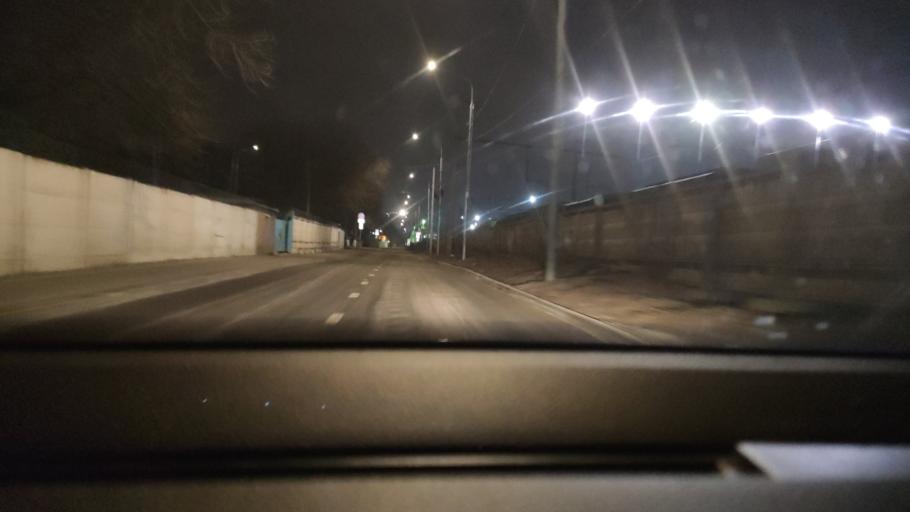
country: RU
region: Moscow
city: Lyublino
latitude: 55.6771
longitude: 37.7331
